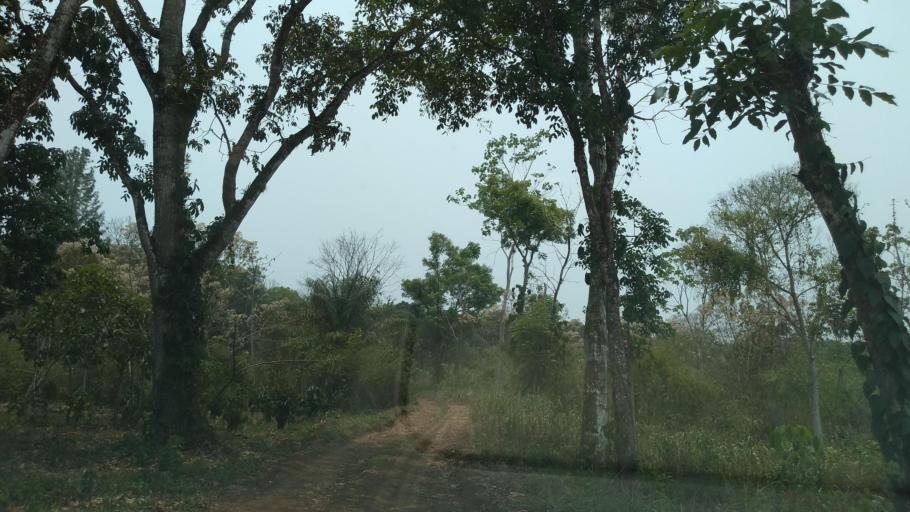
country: MX
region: Veracruz
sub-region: Tezonapa
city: Laguna Chica (Pueblo Nuevo)
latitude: 18.5110
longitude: -96.7623
